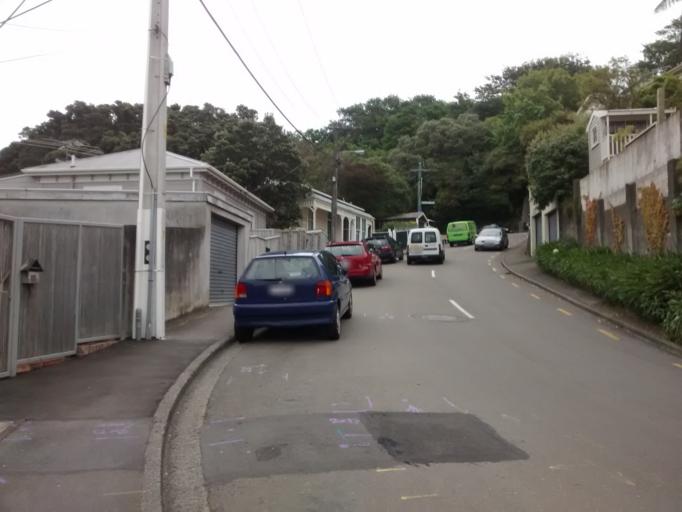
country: NZ
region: Wellington
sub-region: Wellington City
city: Wellington
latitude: -41.2974
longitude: 174.7689
